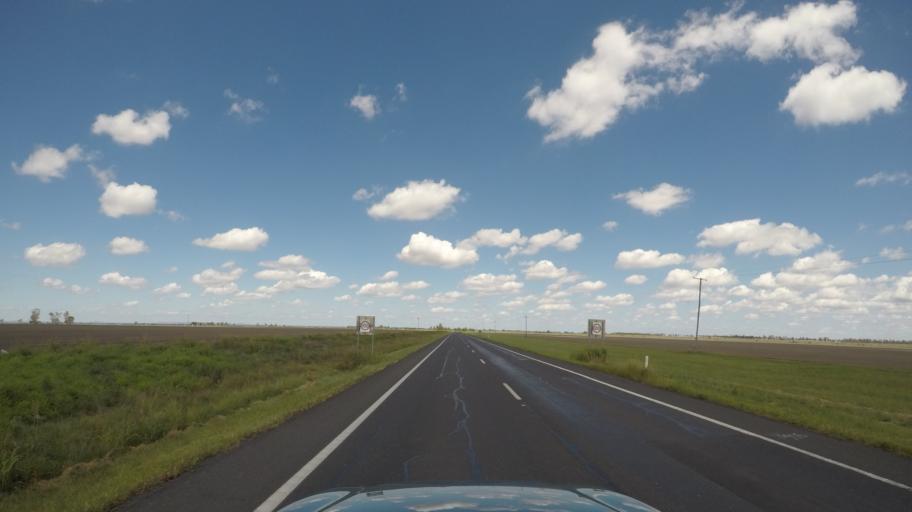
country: AU
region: Queensland
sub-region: Toowoomba
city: Westbrook
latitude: -27.7531
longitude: 151.5264
